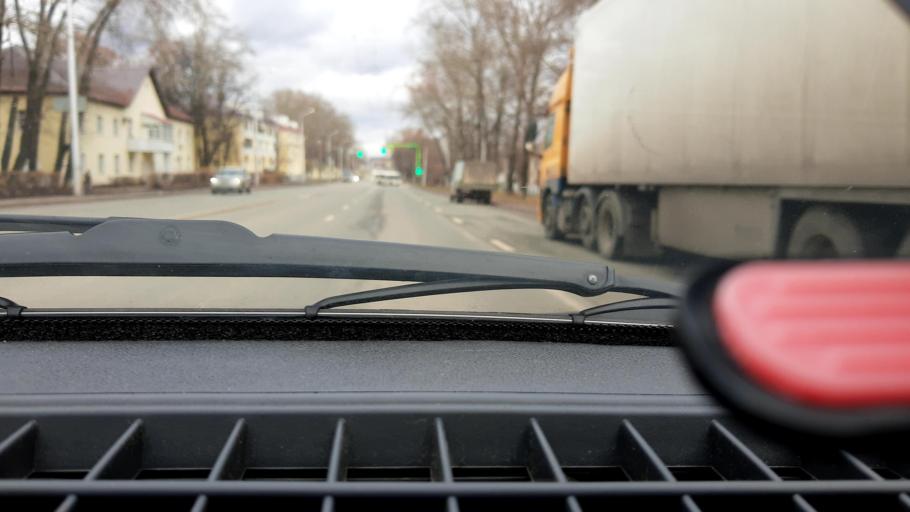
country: RU
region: Bashkortostan
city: Ufa
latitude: 54.8213
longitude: 56.1097
